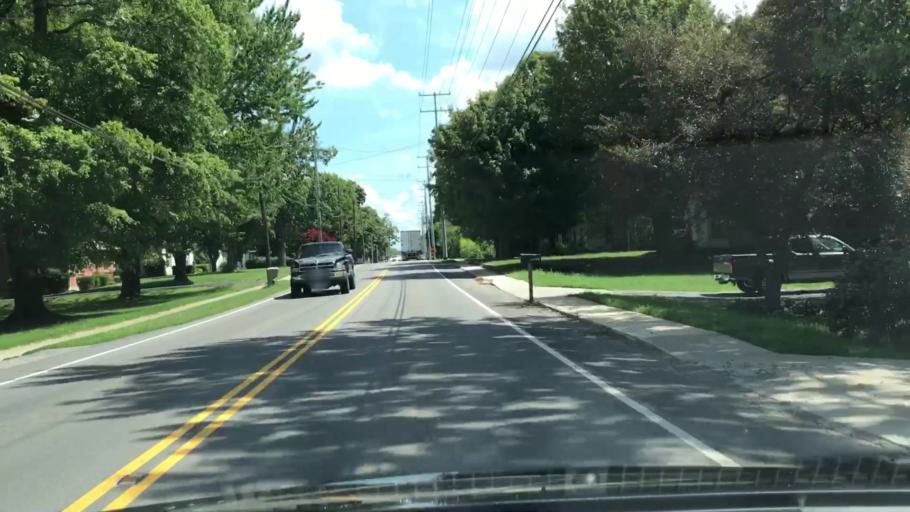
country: US
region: Tennessee
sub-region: Robertson County
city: Cross Plains
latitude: 36.5489
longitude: -86.7011
